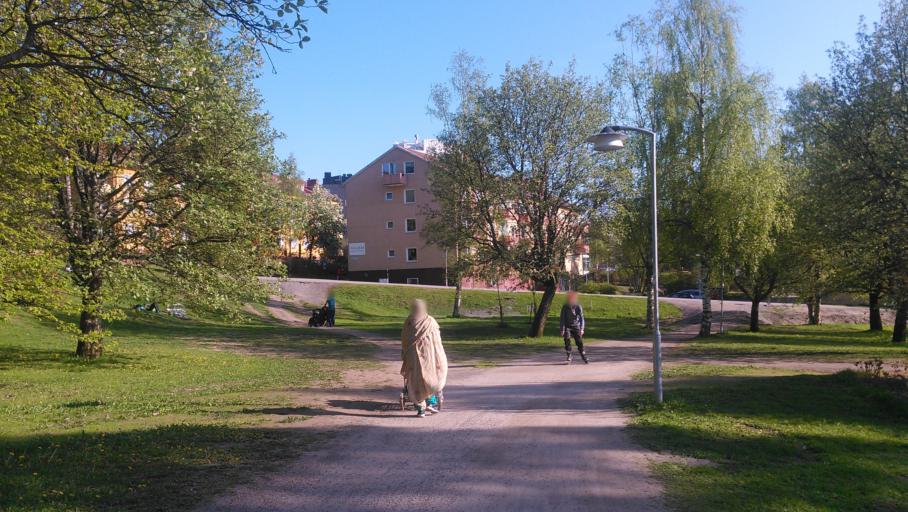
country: SE
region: Vaesterbotten
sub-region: Umea Kommun
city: Umea
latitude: 63.8158
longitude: 20.2978
